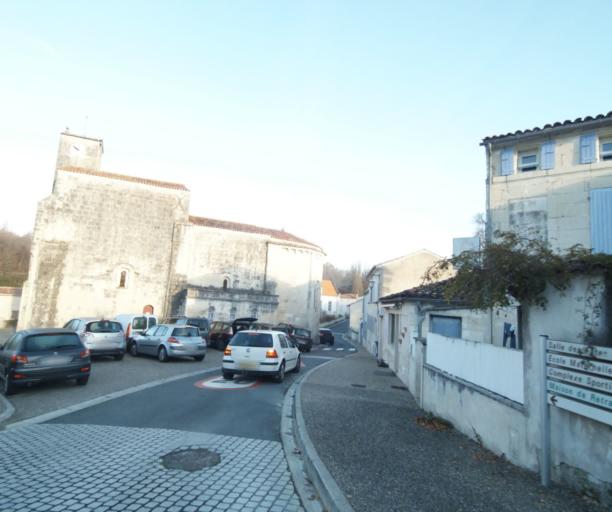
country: FR
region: Poitou-Charentes
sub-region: Departement de la Charente-Maritime
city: Fontcouverte
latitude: 45.7716
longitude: -0.5921
